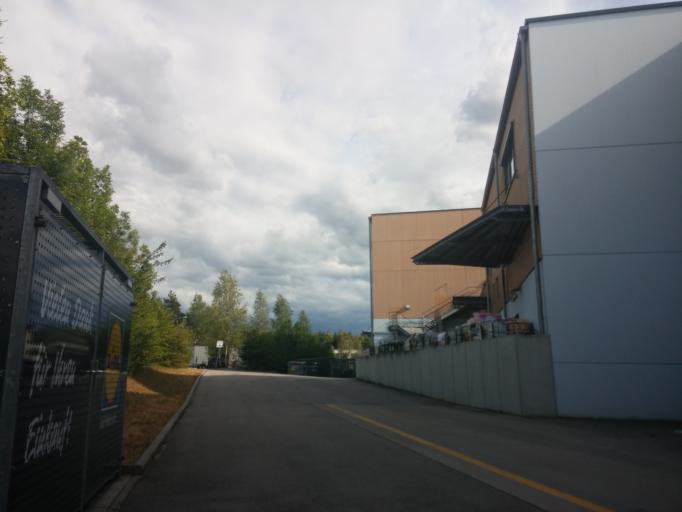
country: DE
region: Bavaria
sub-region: Upper Bavaria
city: Ottobrunn
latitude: 48.0409
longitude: 11.6627
